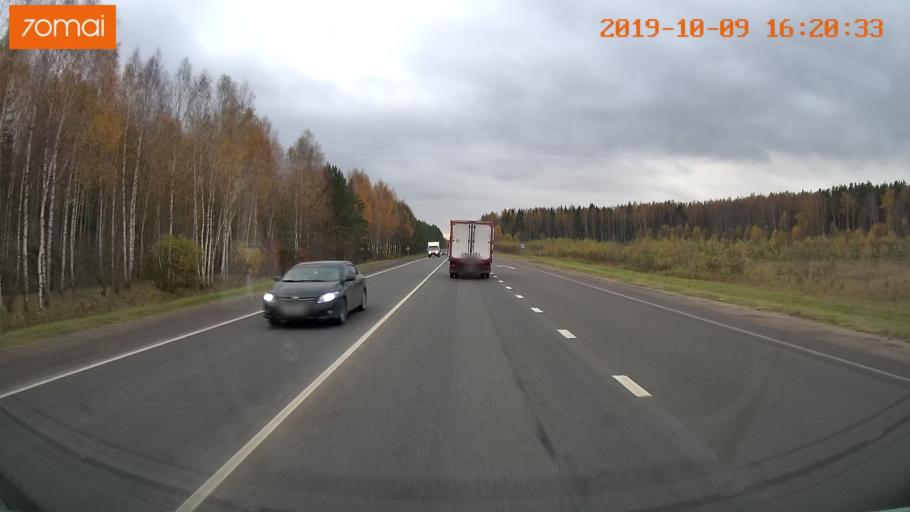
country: RU
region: Kostroma
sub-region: Kostromskoy Rayon
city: Kostroma
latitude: 57.7050
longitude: 40.8919
